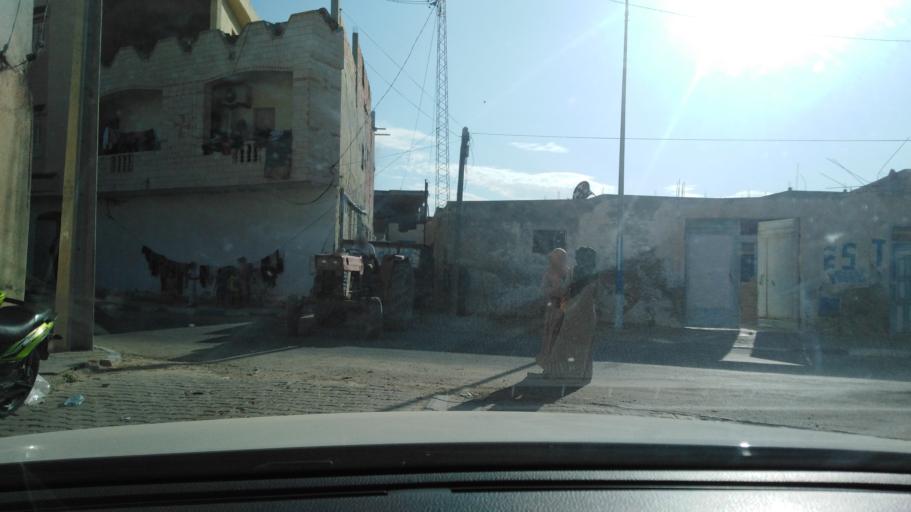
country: TN
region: Qabis
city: Gabes
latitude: 33.9386
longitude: 10.0693
